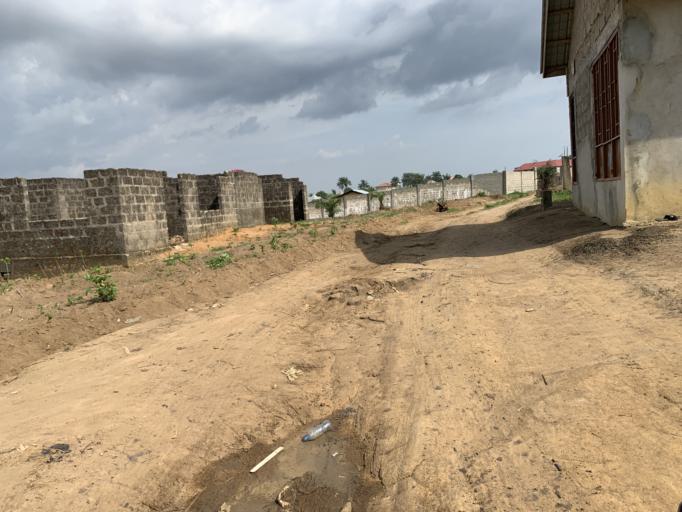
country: SL
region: Western Area
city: Waterloo
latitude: 8.3508
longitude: -13.0353
